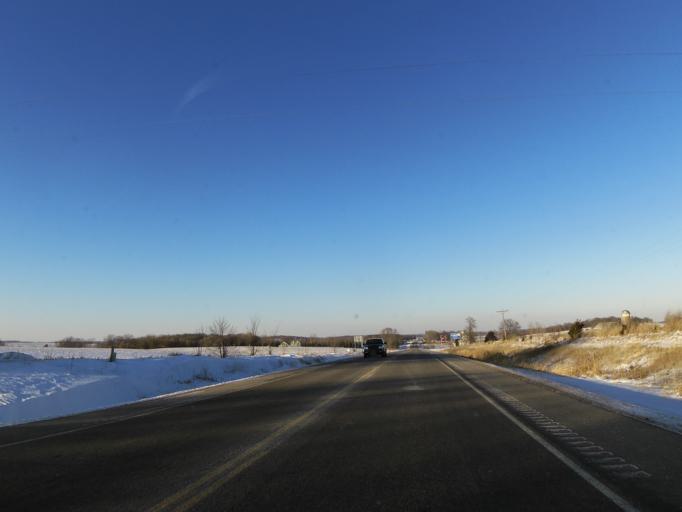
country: US
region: Minnesota
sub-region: Rice County
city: Lonsdale
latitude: 44.5231
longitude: -93.4429
